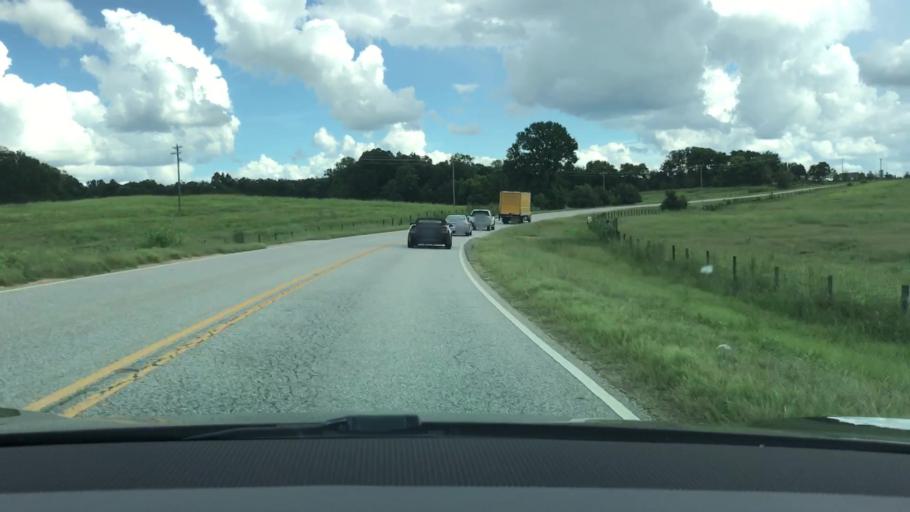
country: US
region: Alabama
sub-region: Montgomery County
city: Pike Road
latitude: 32.2546
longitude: -86.0944
